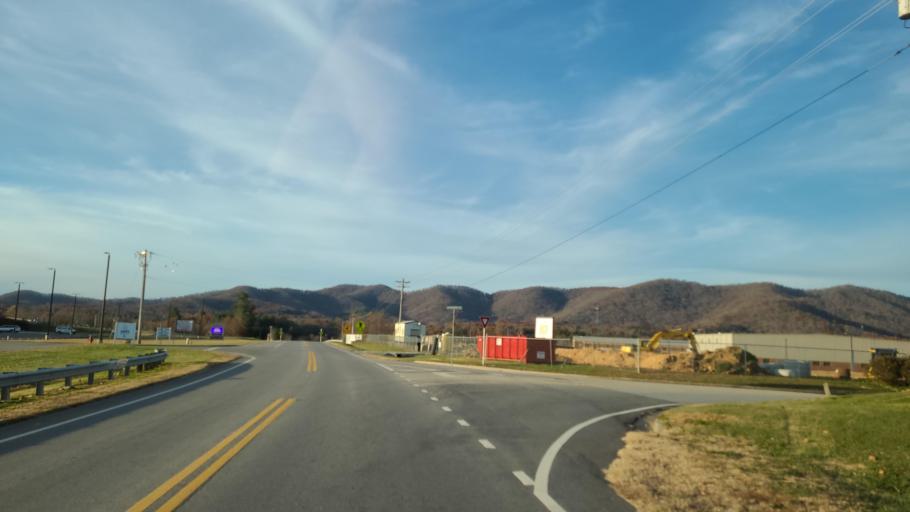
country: US
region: Georgia
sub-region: Union County
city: Blairsville
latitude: 34.8769
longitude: -83.9466
